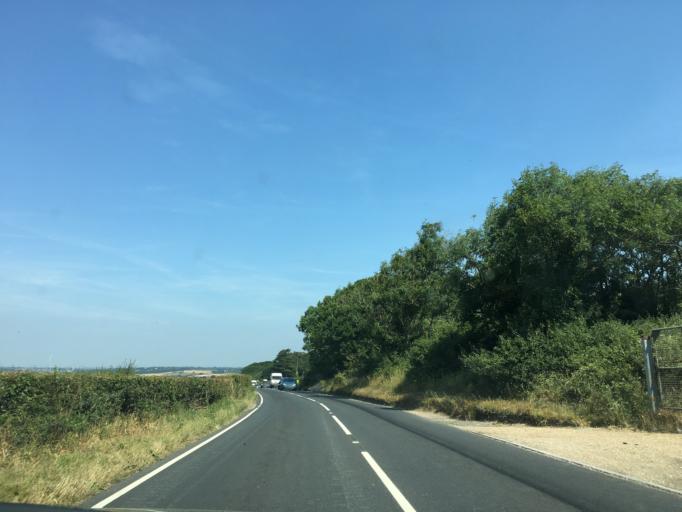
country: GB
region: England
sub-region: Isle of Wight
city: Newchurch
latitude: 50.6979
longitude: -1.2408
